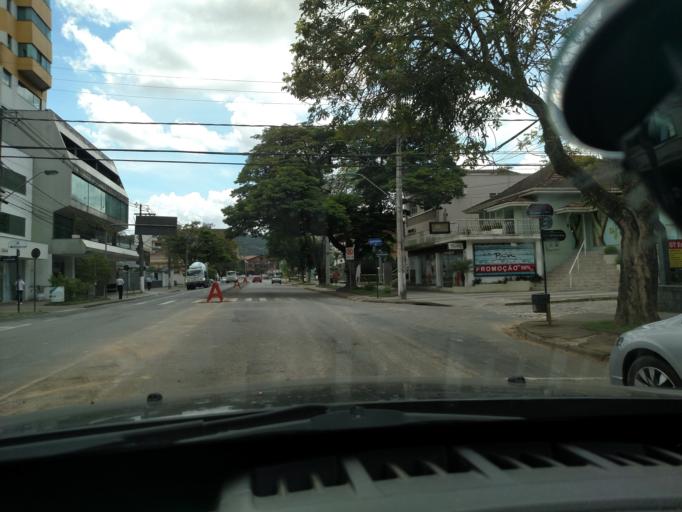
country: BR
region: Santa Catarina
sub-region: Blumenau
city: Blumenau
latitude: -26.9252
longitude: -49.0612
